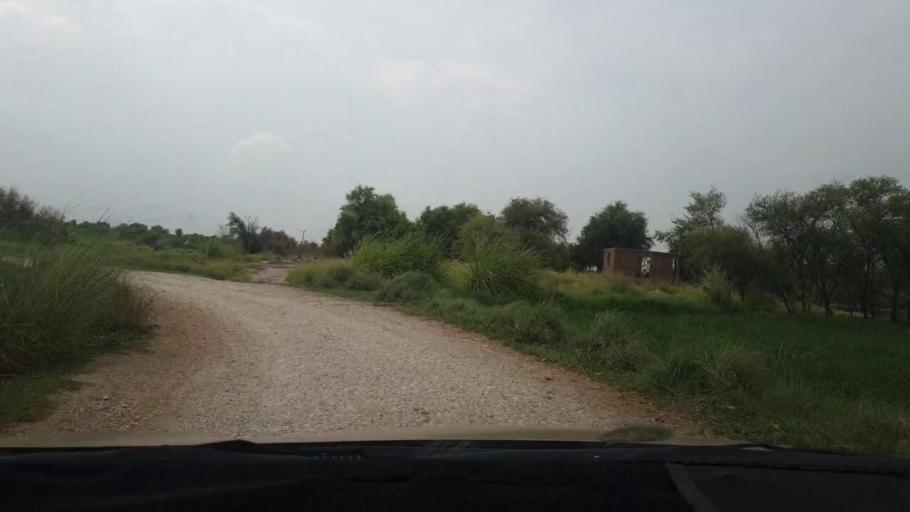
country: PK
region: Sindh
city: Naudero
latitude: 27.6364
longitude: 68.3074
